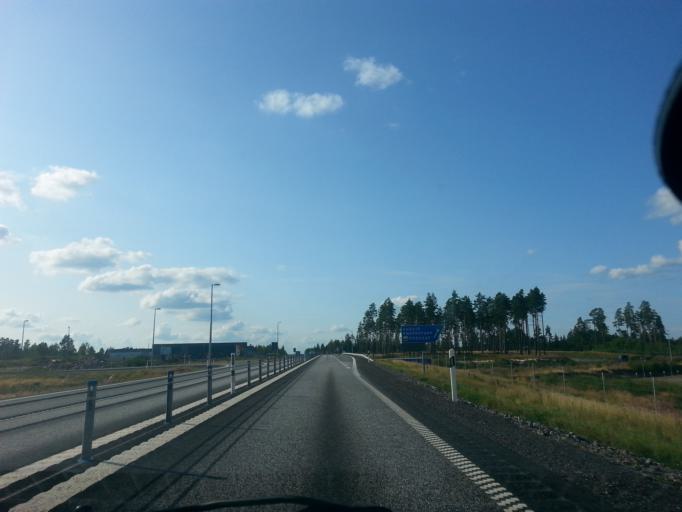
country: SE
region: Joenkoeping
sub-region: Gislaveds Kommun
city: Gislaved
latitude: 57.2822
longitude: 13.6089
